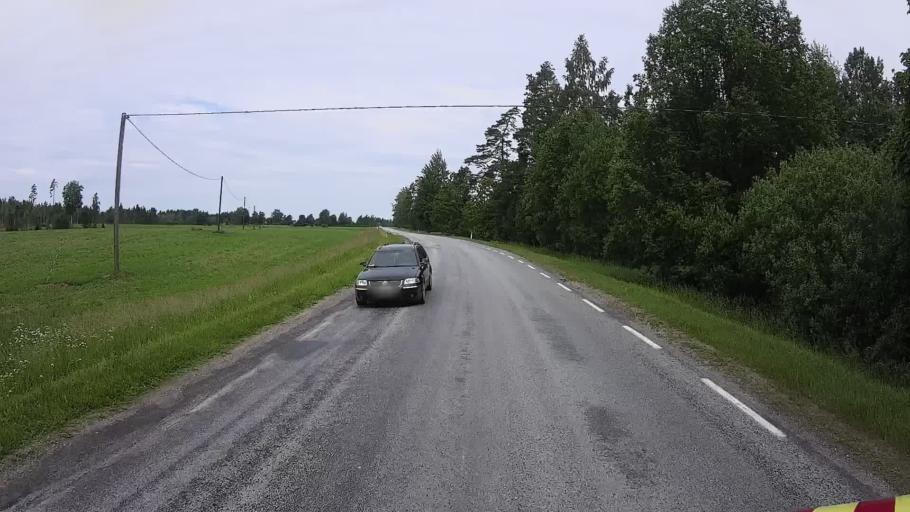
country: EE
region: Viljandimaa
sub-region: Karksi vald
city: Karksi-Nuia
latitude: 58.2235
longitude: 25.6144
